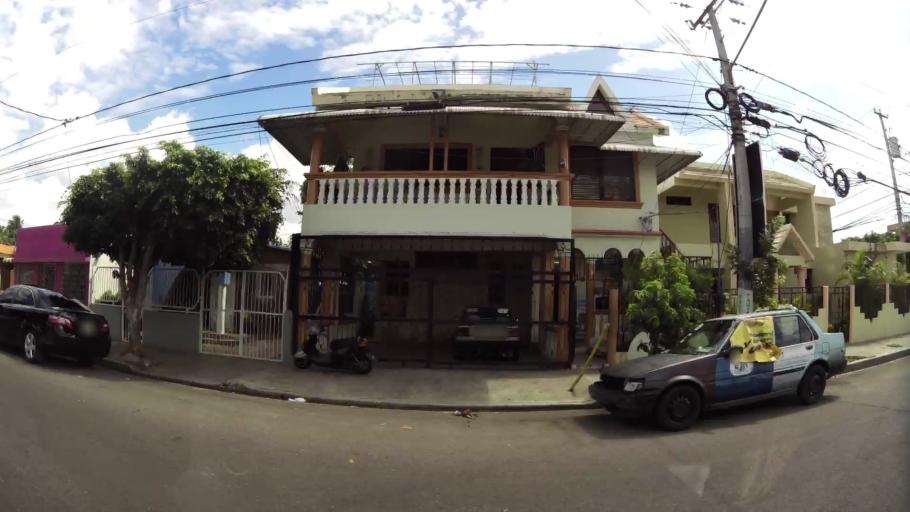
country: DO
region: Santiago
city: Santiago de los Caballeros
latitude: 19.4655
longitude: -70.7002
